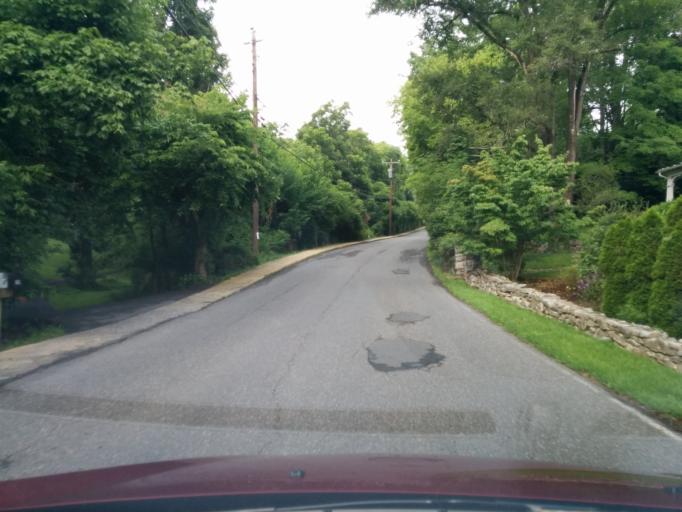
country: US
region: Virginia
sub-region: City of Lexington
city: Lexington
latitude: 37.7869
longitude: -79.4540
